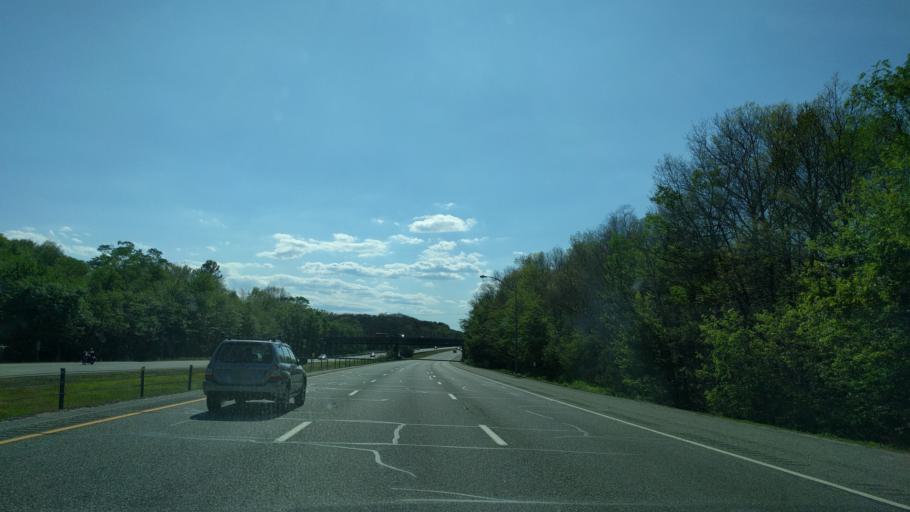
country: US
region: Rhode Island
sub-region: Providence County
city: Cumberland
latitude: 41.9508
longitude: -71.3996
